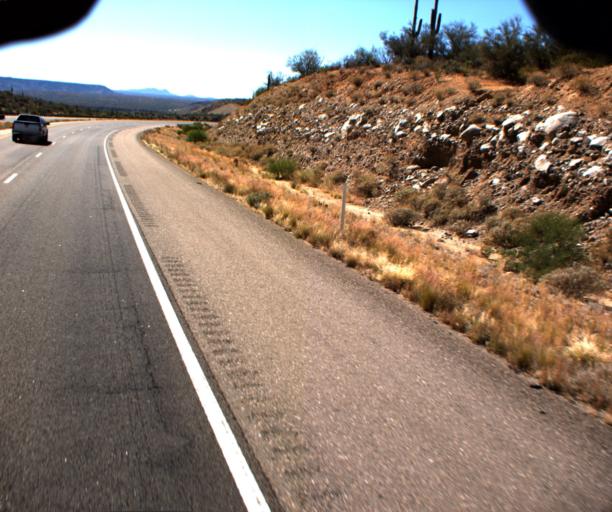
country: US
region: Arizona
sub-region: Yavapai County
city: Bagdad
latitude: 34.3955
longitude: -113.2120
